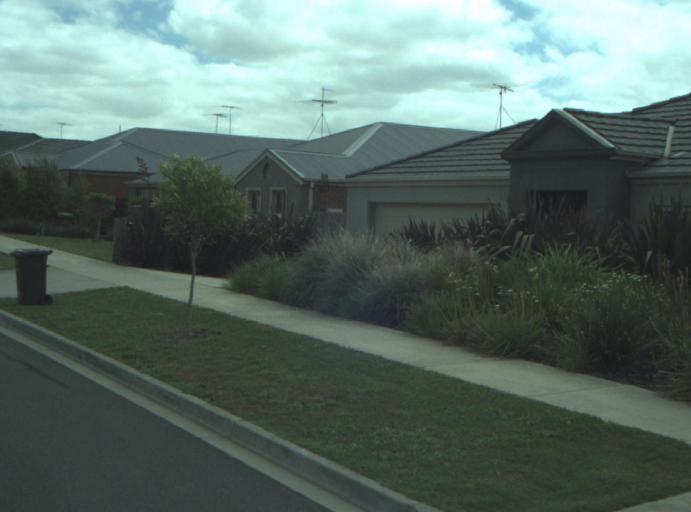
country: AU
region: Victoria
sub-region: Greater Geelong
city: Wandana Heights
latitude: -38.1969
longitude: 144.3088
